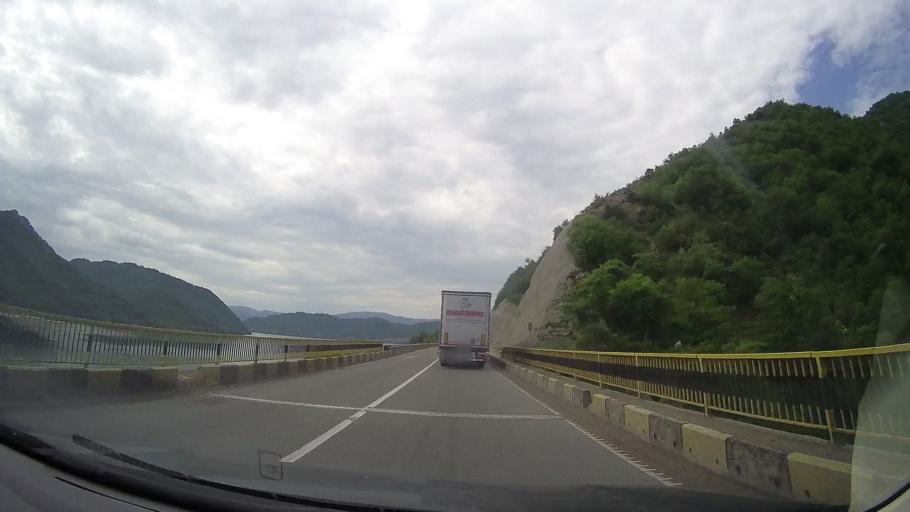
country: RO
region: Mehedinti
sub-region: Comuna Ilovita
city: Ilovita
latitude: 44.7028
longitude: 22.4964
